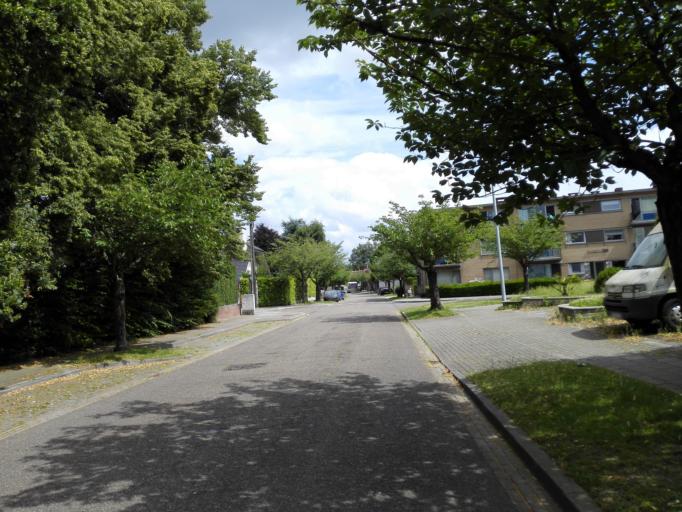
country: BE
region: Flanders
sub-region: Provincie Vlaams-Brabant
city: Leuven
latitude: 50.8675
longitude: 4.7312
